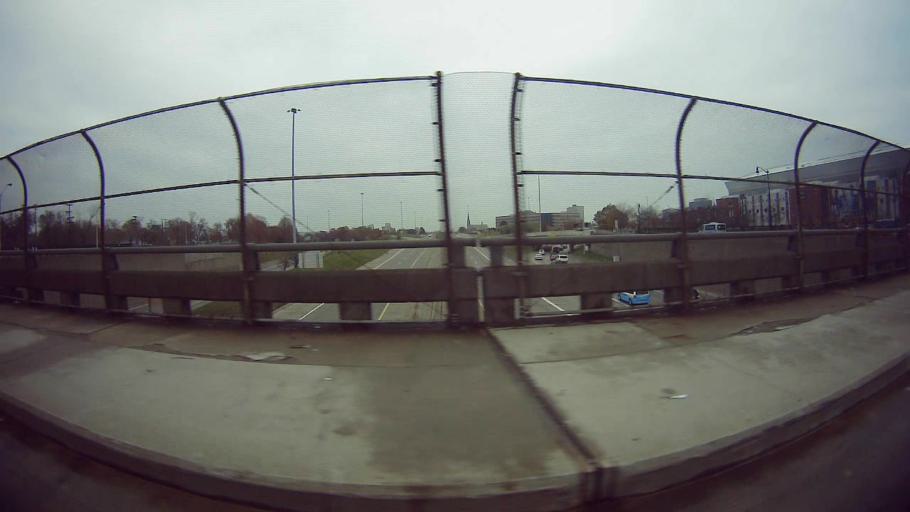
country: US
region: Michigan
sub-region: Wayne County
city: Detroit
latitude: 42.3420
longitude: -83.0494
